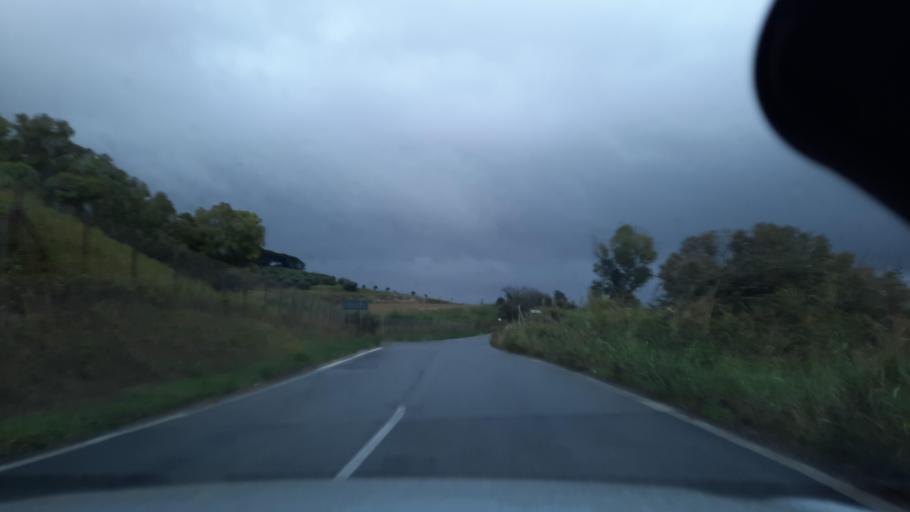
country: IT
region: Latium
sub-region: Citta metropolitana di Roma Capitale
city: Ponte Galeria-La Pisana
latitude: 41.8187
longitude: 12.3558
